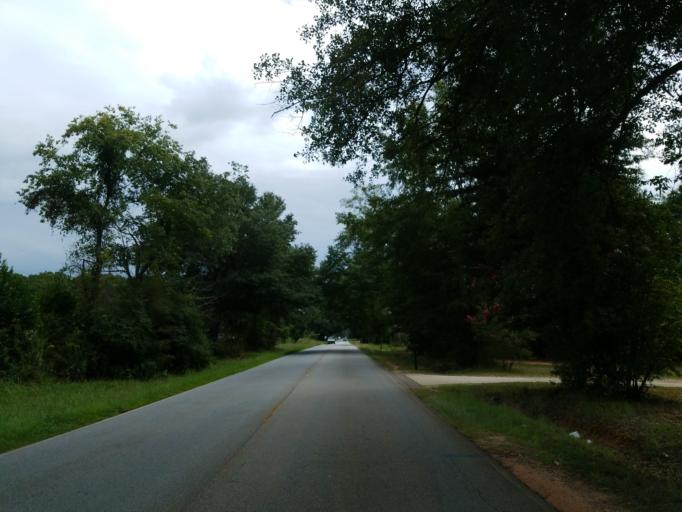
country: US
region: Georgia
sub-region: Spalding County
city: Experiment
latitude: 33.2858
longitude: -84.2846
